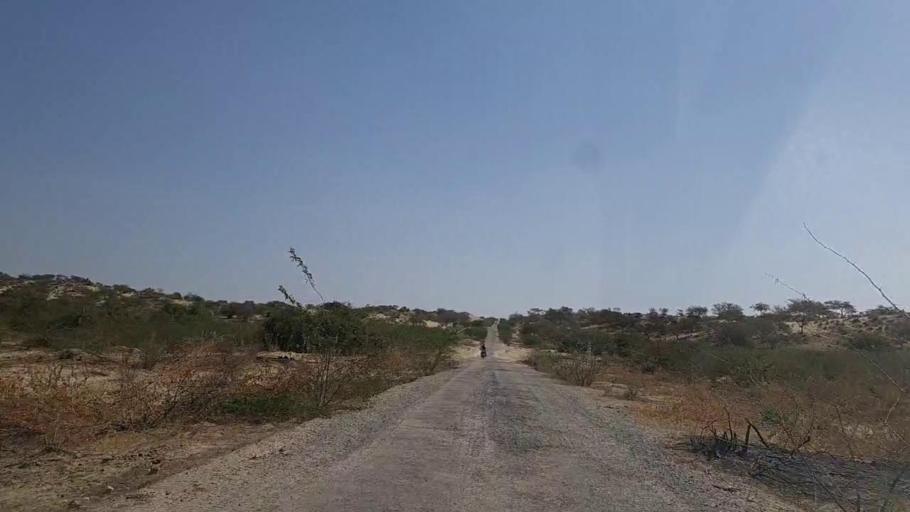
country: PK
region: Sindh
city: Diplo
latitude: 24.4887
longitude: 69.4422
